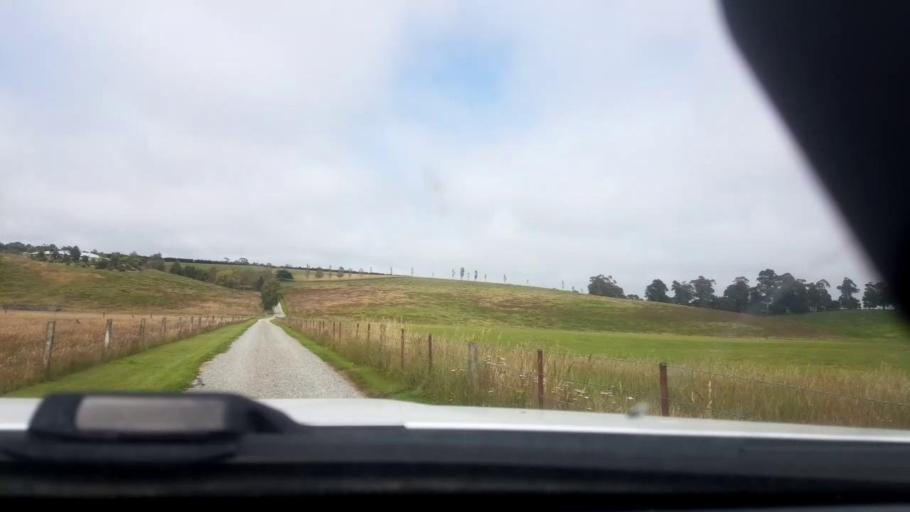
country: NZ
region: Canterbury
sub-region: Timaru District
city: Pleasant Point
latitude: -44.3218
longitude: 171.1920
